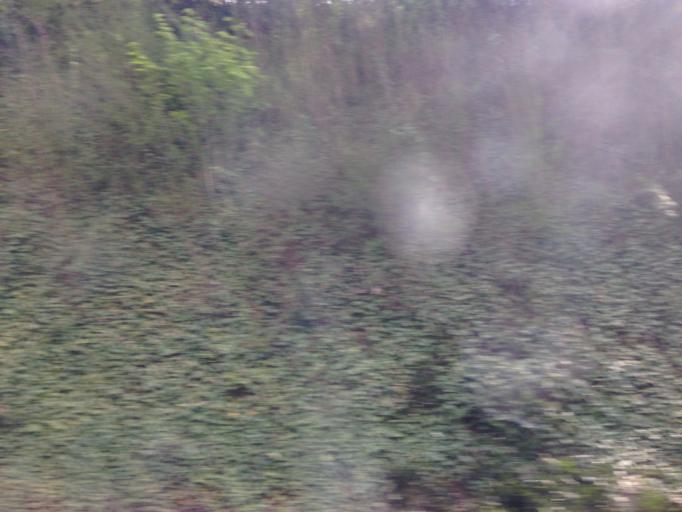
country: GB
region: England
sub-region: Greater London
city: Carshalton
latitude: 51.3612
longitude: -0.1826
